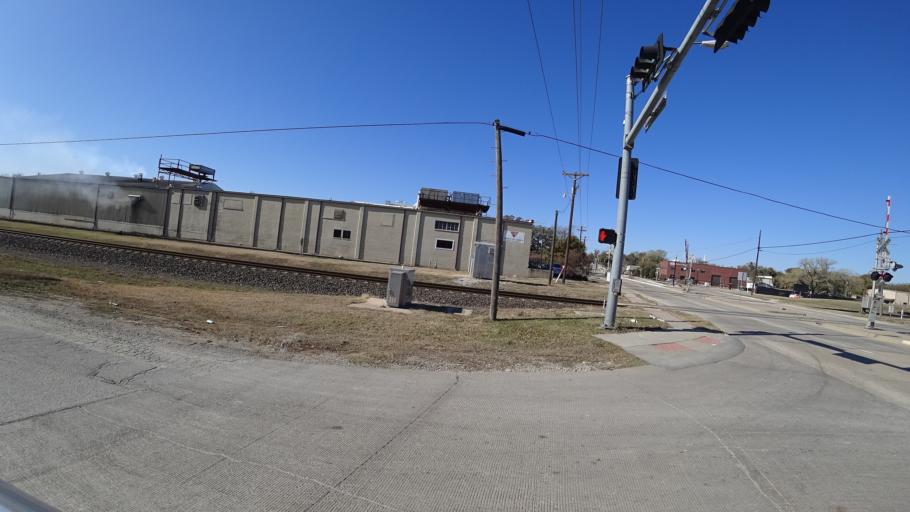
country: US
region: Texas
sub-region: Denton County
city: Lewisville
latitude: 33.0462
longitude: -96.9857
